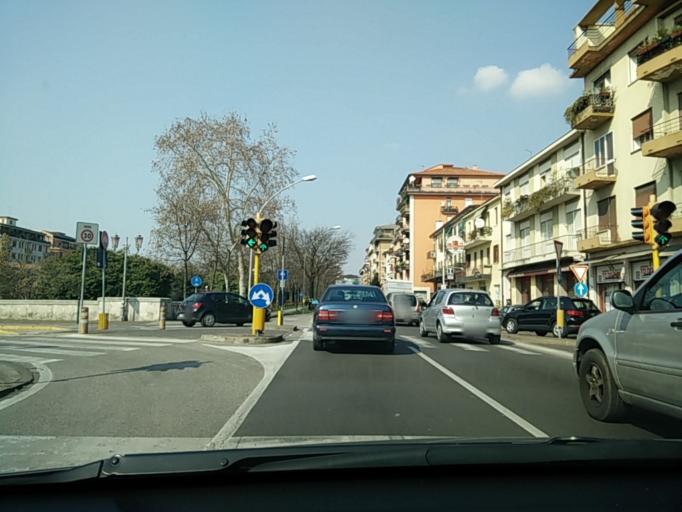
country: IT
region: Veneto
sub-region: Provincia di Treviso
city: Treviso
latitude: 45.6658
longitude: 12.2554
